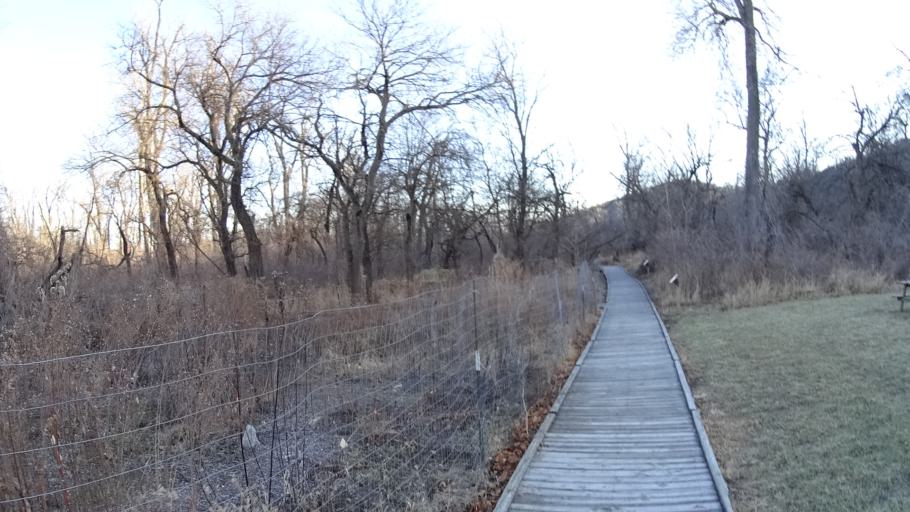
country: US
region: Nebraska
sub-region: Sarpy County
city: Bellevue
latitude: 41.1747
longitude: -95.8903
